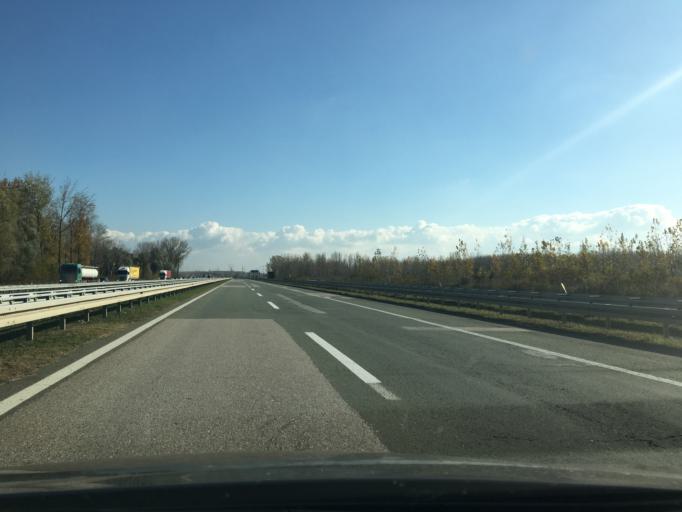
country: RS
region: Autonomna Pokrajina Vojvodina
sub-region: Juznobacki Okrug
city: Petrovaradin
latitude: 45.2925
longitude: 19.8827
